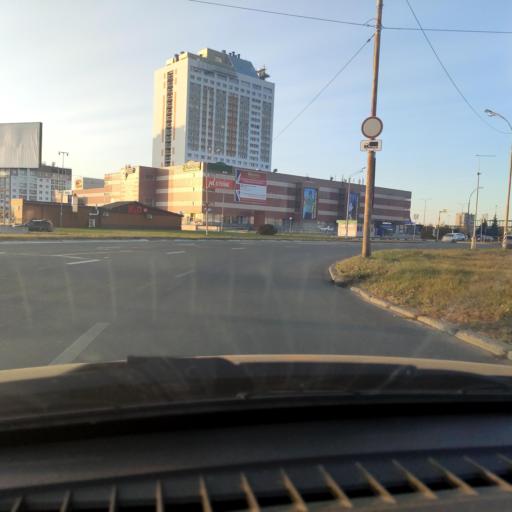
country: RU
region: Samara
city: Tol'yatti
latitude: 53.4998
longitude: 49.2751
